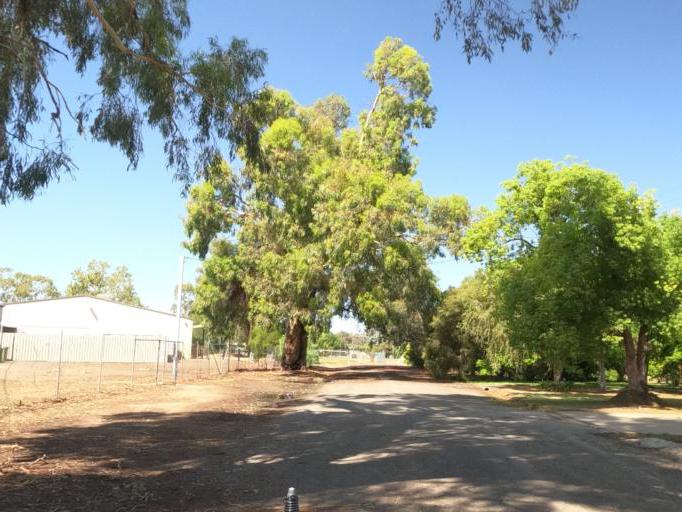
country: AU
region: New South Wales
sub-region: Corowa Shire
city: Mulwala
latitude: -35.9877
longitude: 146.0011
